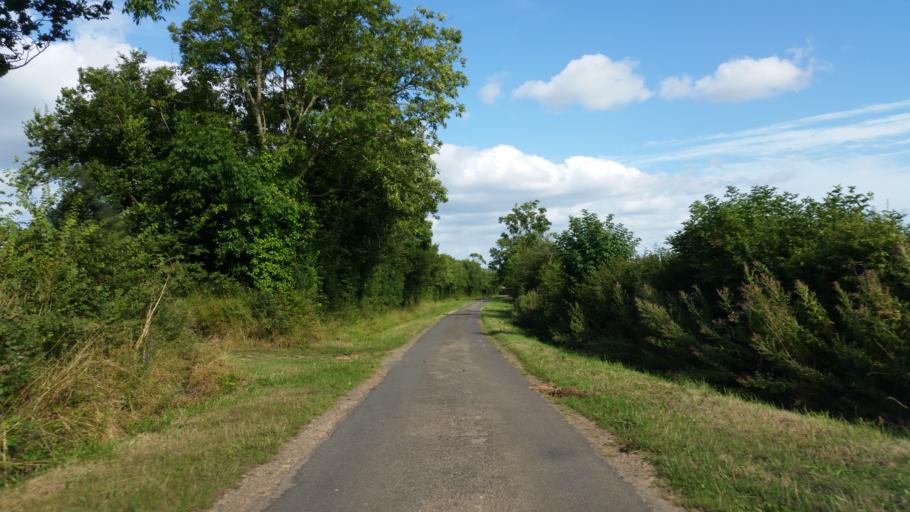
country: FR
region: Lower Normandy
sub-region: Departement de la Manche
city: Sainte-Mere-Eglise
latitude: 49.4517
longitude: -1.2816
